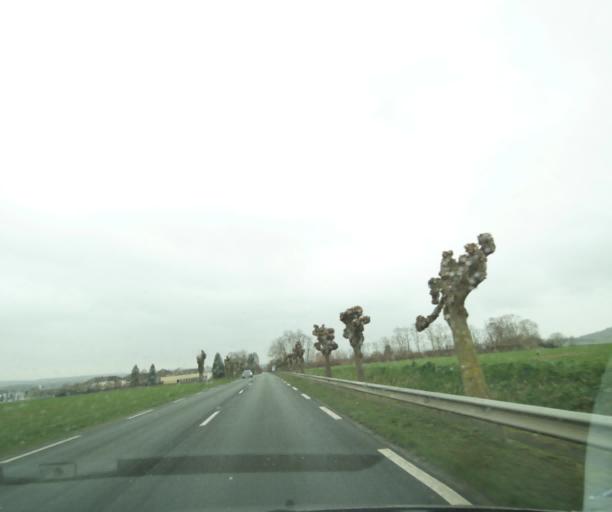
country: FR
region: Picardie
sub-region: Departement de l'Oise
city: Noyon
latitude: 49.5921
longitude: 3.0037
